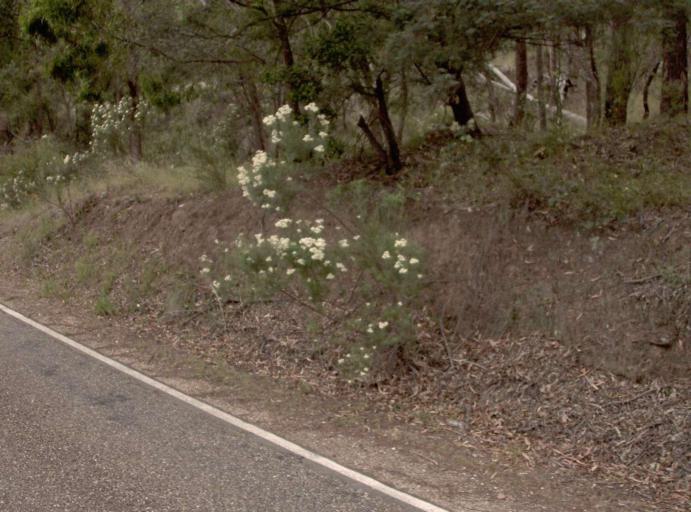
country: AU
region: Victoria
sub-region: East Gippsland
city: Bairnsdale
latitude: -37.5360
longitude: 147.2121
